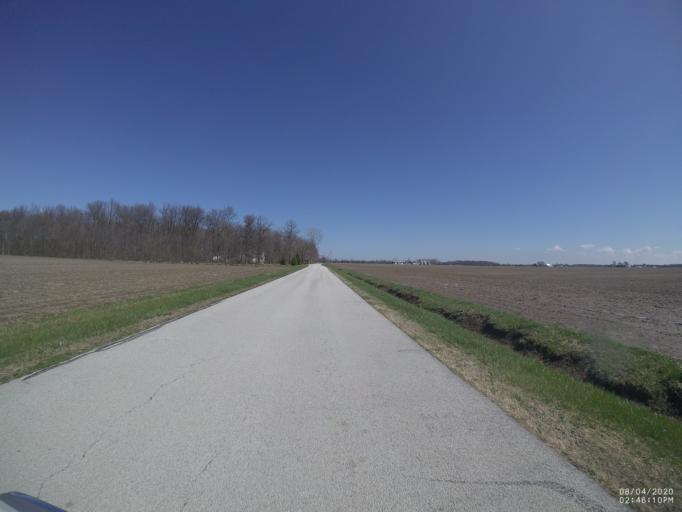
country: US
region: Ohio
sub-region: Sandusky County
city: Gibsonburg
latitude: 41.2974
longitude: -83.2834
